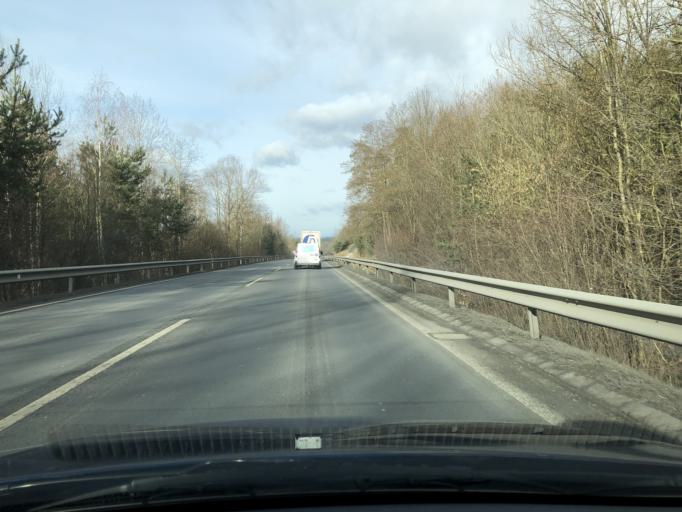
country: AT
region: Burgenland
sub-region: Politischer Bezirk Oberwart
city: Oberwart
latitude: 47.2753
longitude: 16.1993
